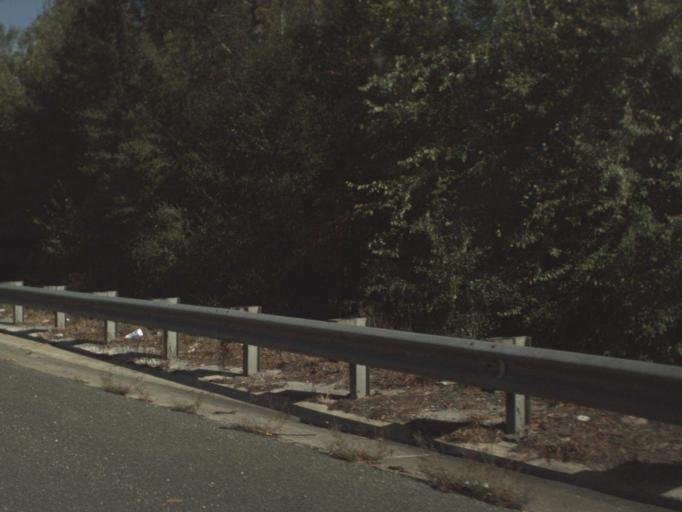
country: US
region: Florida
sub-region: Gadsden County
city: Havana
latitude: 30.5568
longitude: -84.3860
